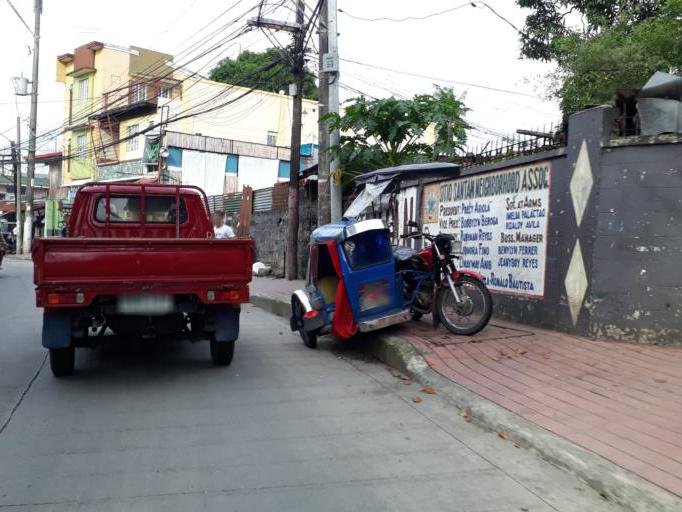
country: PH
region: Calabarzon
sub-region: Province of Rizal
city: Valenzuela
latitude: 14.6768
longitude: 120.9886
